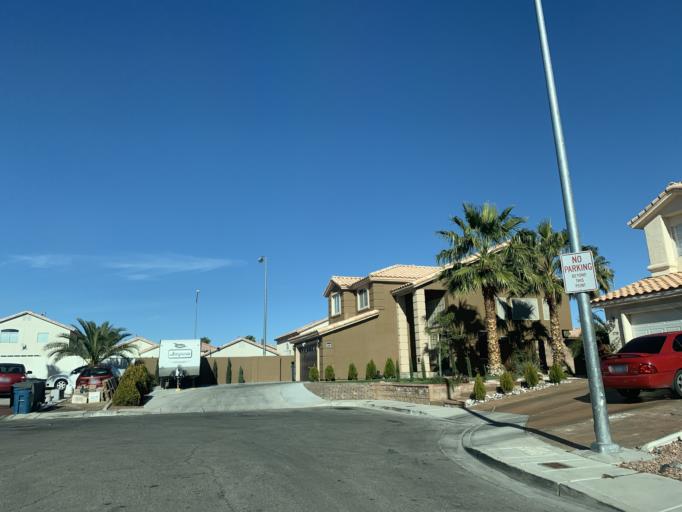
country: US
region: Nevada
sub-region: Clark County
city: Summerlin South
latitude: 36.1220
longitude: -115.3008
